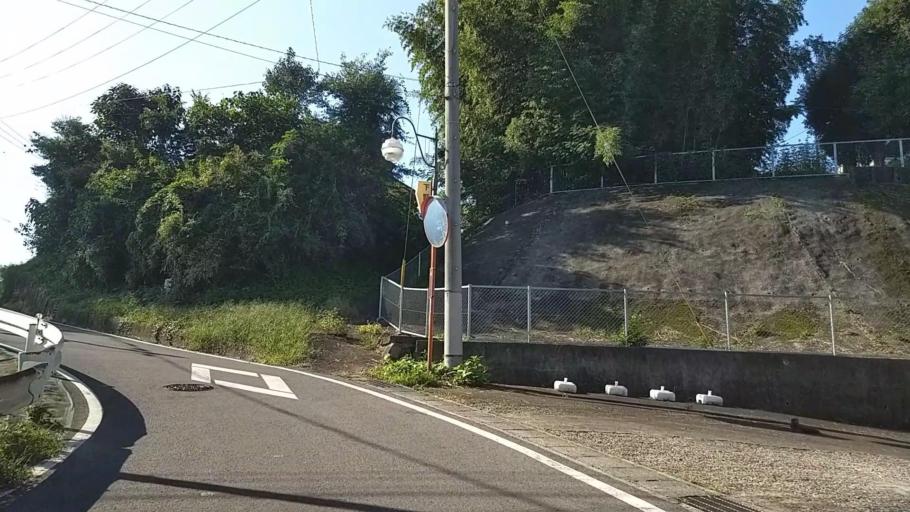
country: JP
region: Gunma
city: Annaka
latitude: 36.3344
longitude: 138.9091
